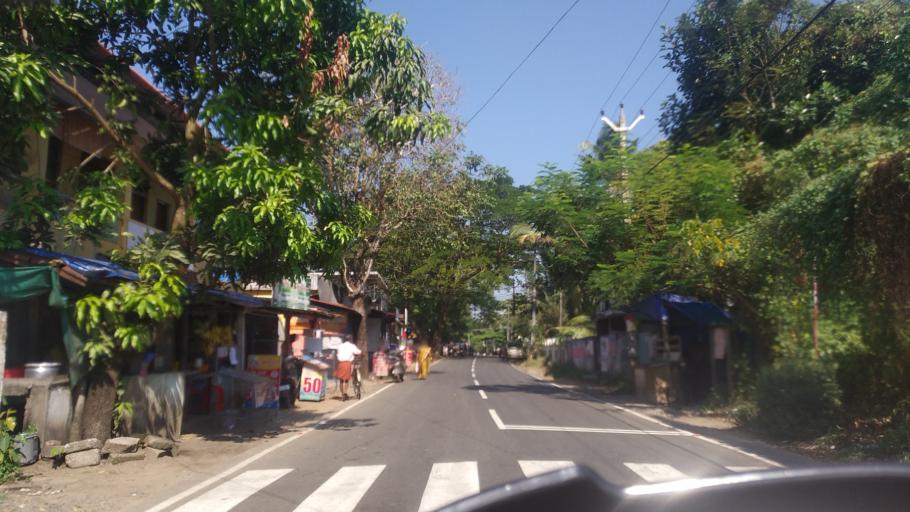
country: IN
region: Kerala
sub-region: Ernakulam
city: Elur
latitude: 10.1183
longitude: 76.2468
